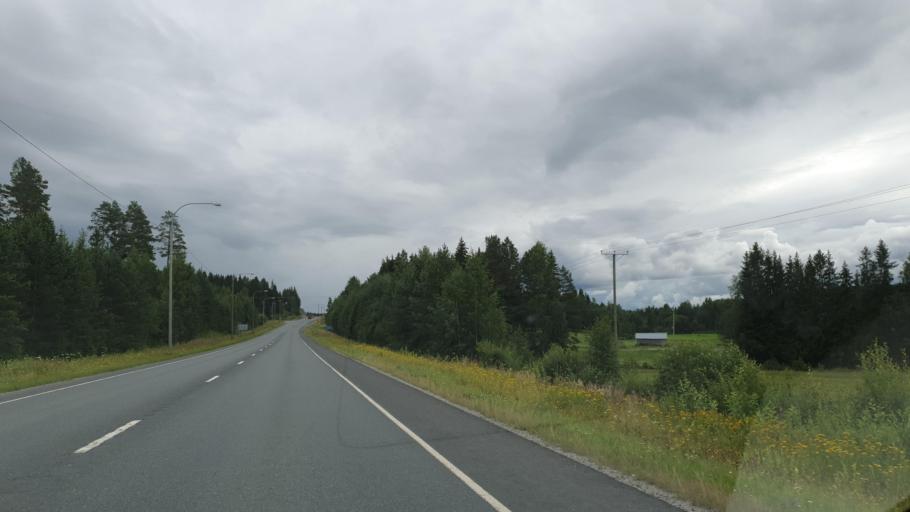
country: FI
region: Northern Savo
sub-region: Ylae-Savo
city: Lapinlahti
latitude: 63.3117
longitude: 27.4476
